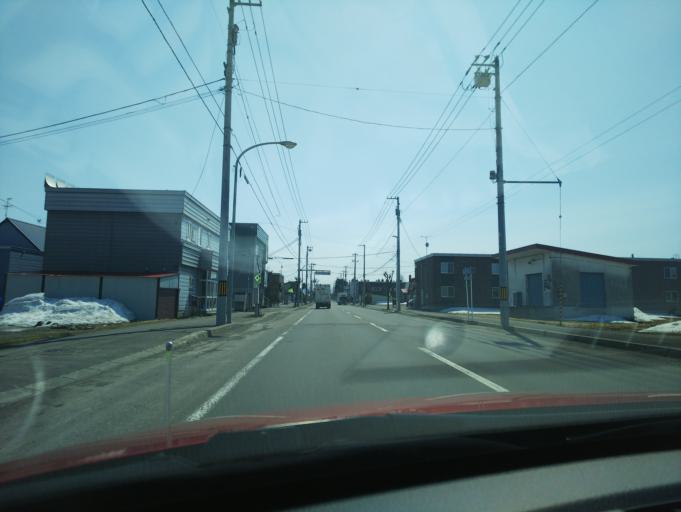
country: JP
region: Hokkaido
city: Nayoro
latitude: 44.3425
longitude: 142.4643
